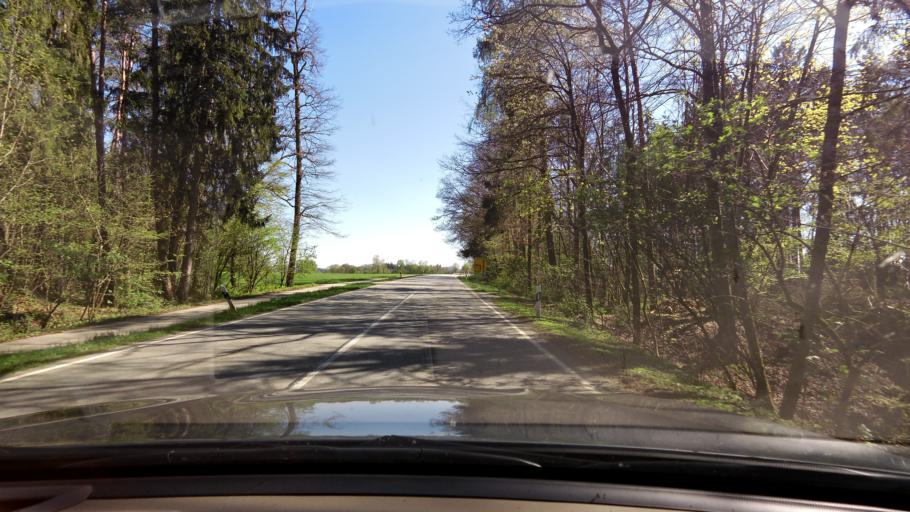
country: DE
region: Bavaria
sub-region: Upper Bavaria
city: Soyen
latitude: 48.1132
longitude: 12.1858
